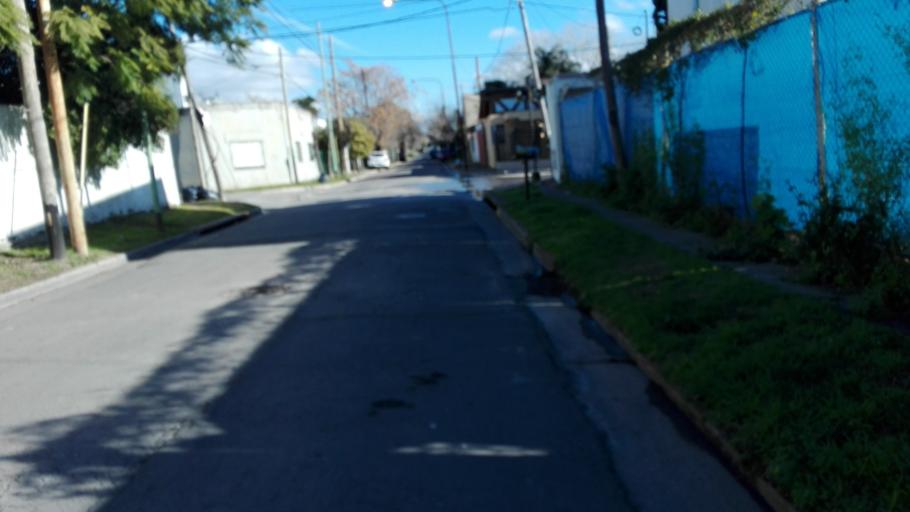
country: AR
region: Buenos Aires
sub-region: Partido de La Plata
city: La Plata
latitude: -34.8840
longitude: -57.9978
